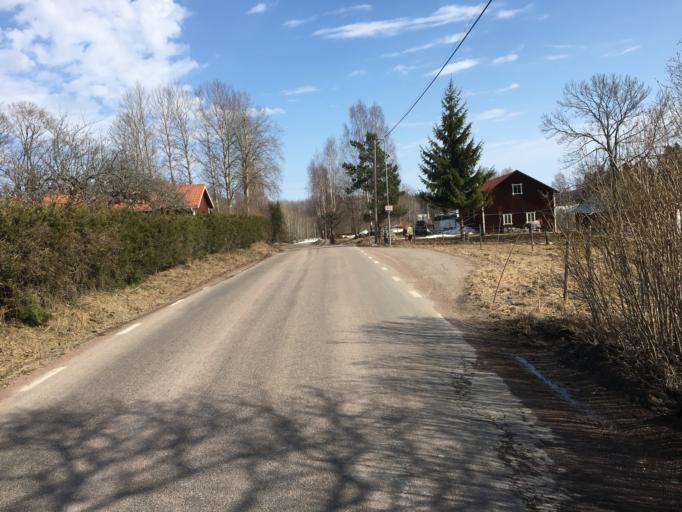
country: SE
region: Gaevleborg
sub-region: Hofors Kommun
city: Hofors
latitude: 60.5146
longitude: 16.4496
